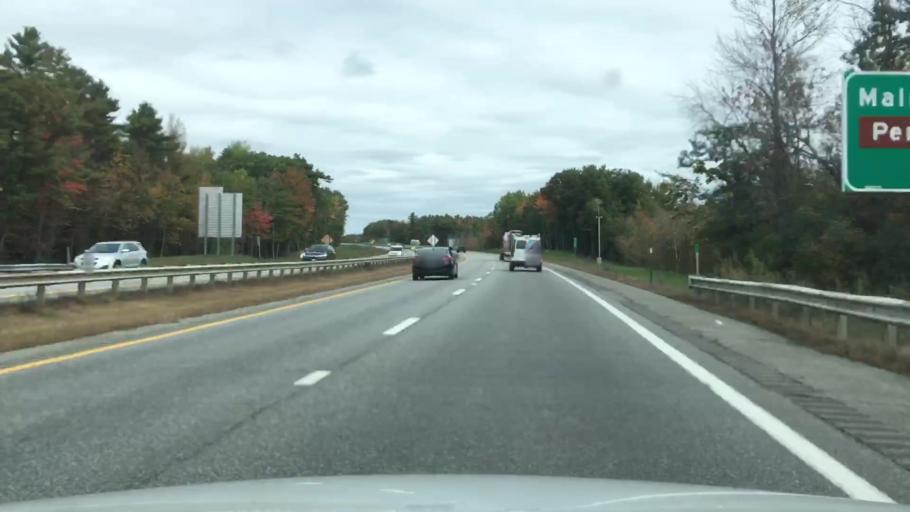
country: US
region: Maine
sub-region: Kennebec County
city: Gardiner
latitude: 44.2351
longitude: -69.8087
